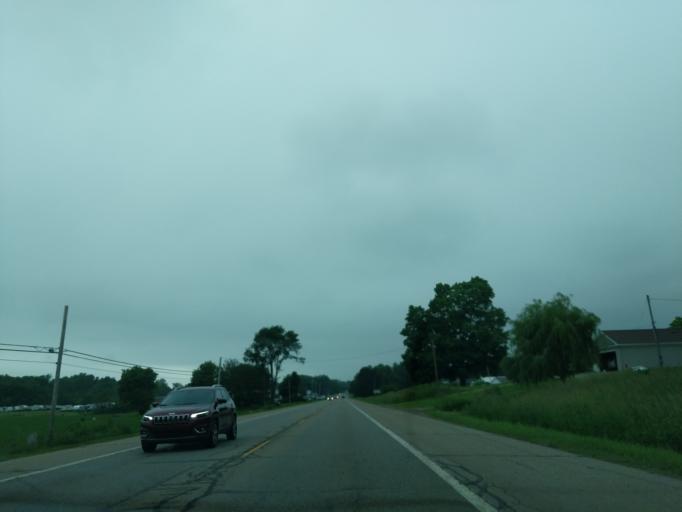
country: US
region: Michigan
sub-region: Branch County
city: Quincy
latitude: 41.9392
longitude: -84.9243
